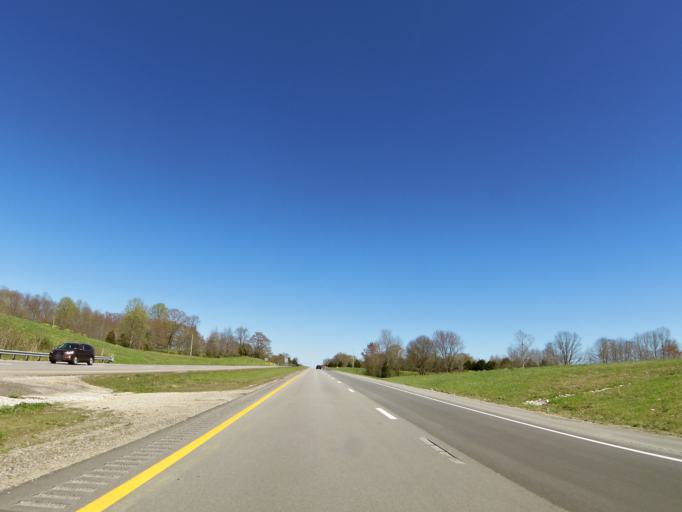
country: US
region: Kentucky
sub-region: Pulaski County
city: Somerset
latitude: 37.0926
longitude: -84.8008
